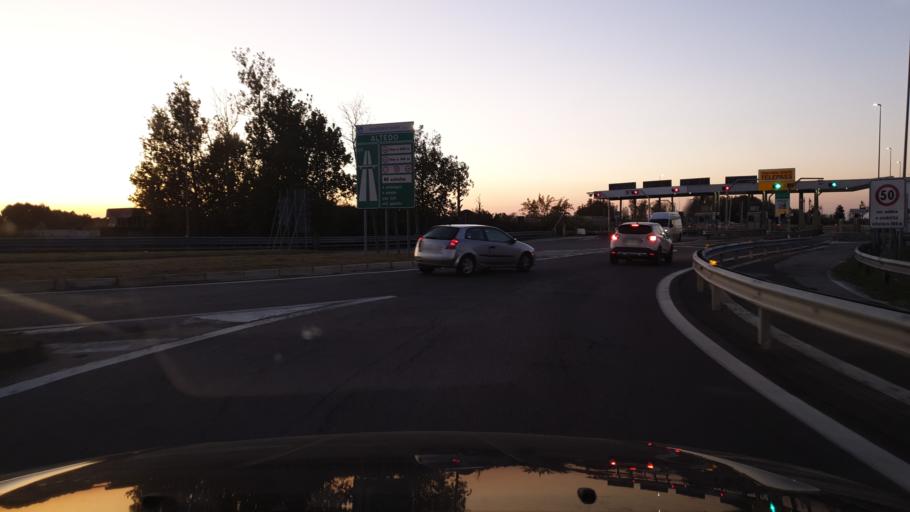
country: IT
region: Emilia-Romagna
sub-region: Provincia di Bologna
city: Altedo
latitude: 44.6849
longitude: 11.4821
